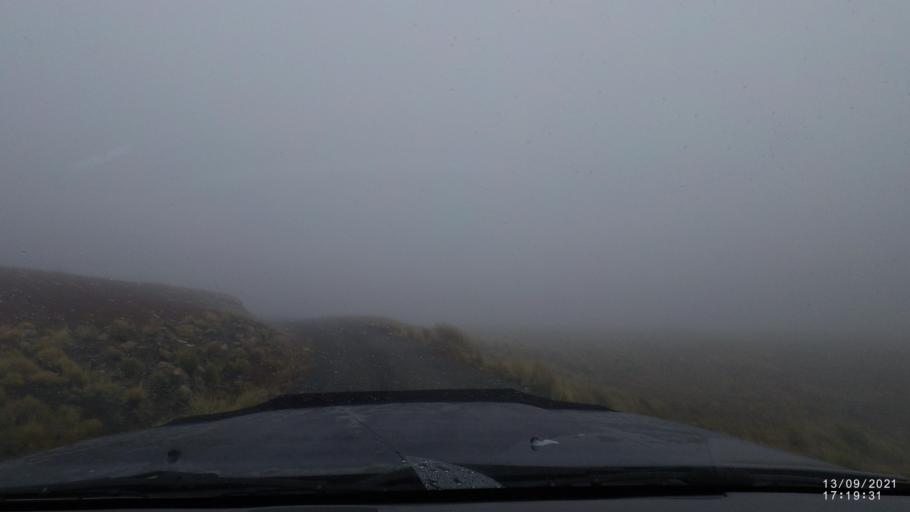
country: BO
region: Cochabamba
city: Colomi
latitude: -17.3497
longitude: -65.7622
